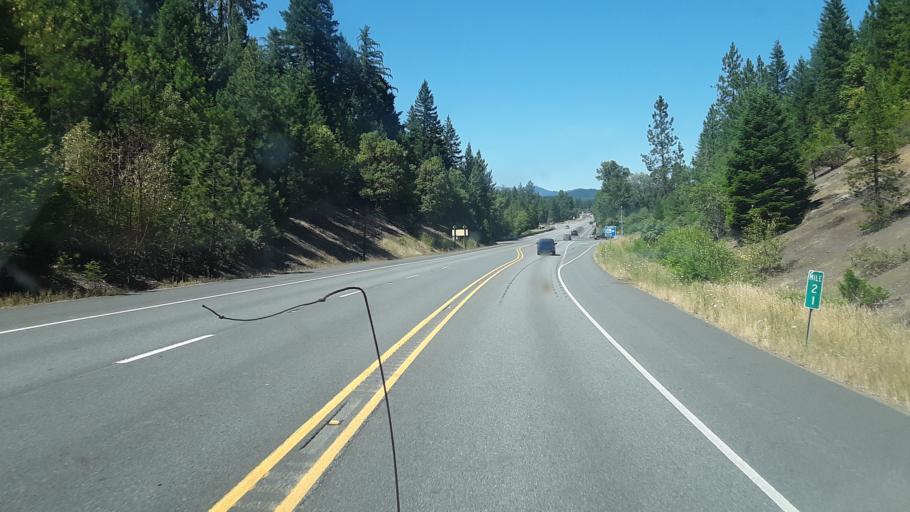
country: US
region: Oregon
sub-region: Josephine County
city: Cave Junction
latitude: 42.2689
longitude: -123.6196
